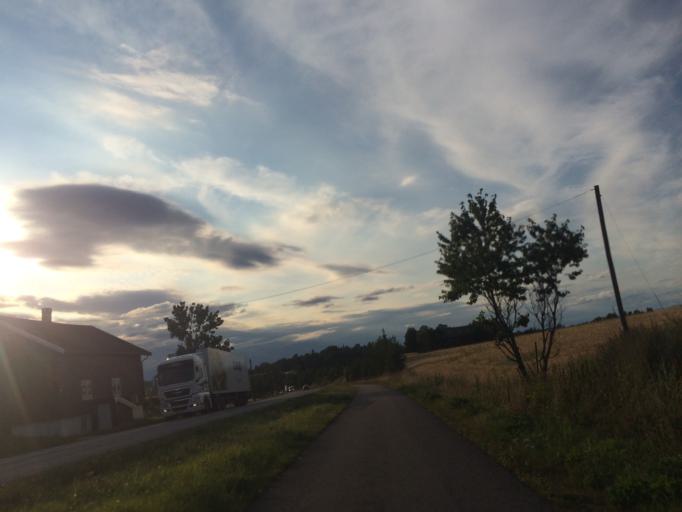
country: NO
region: Ostfold
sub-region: Hobol
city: Elvestad
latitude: 59.6700
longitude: 10.8976
